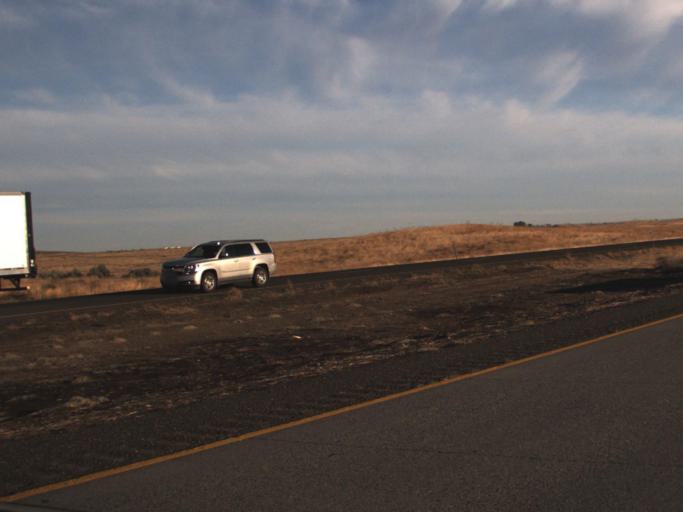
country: US
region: Washington
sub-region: Franklin County
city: Pasco
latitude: 46.4065
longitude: -119.0520
